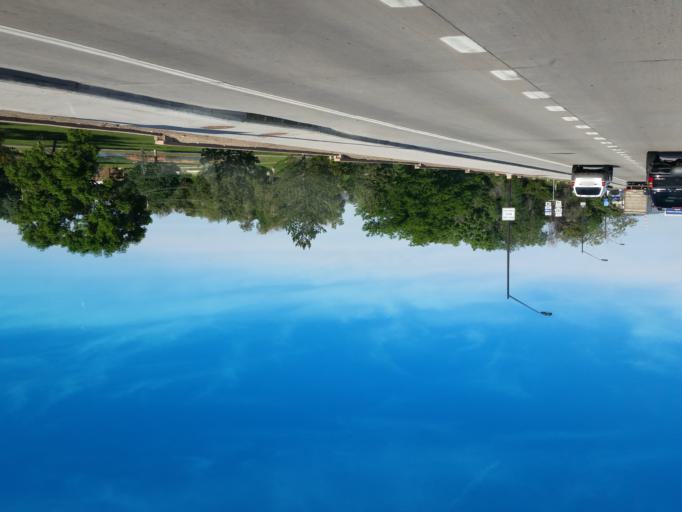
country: US
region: Colorado
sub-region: Larimer County
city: Fort Collins
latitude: 40.5816
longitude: -105.0603
